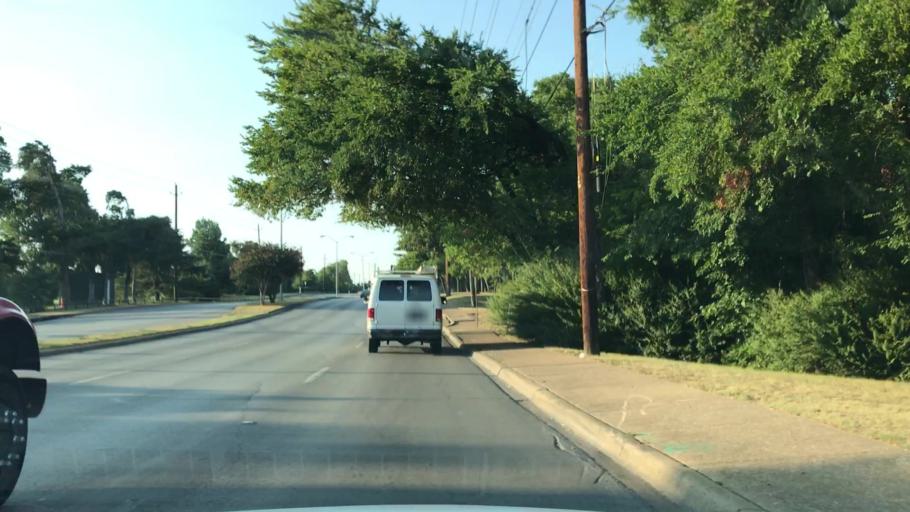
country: US
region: Texas
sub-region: Dallas County
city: Cockrell Hill
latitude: 32.7559
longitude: -96.8566
